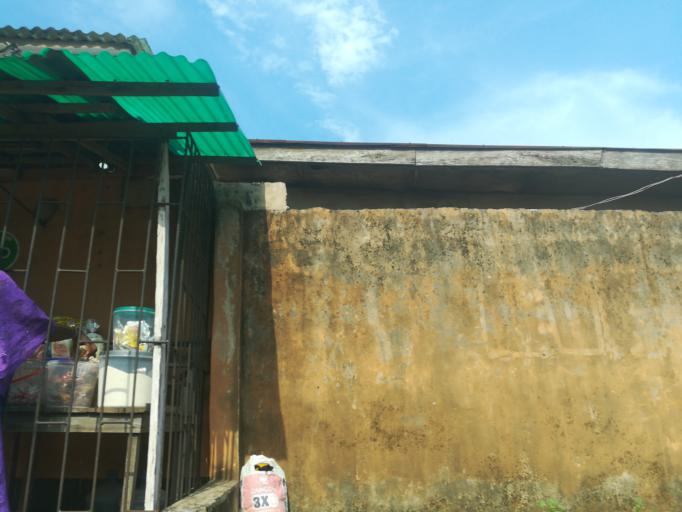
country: NG
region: Lagos
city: Ikorodu
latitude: 6.6310
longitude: 3.5218
